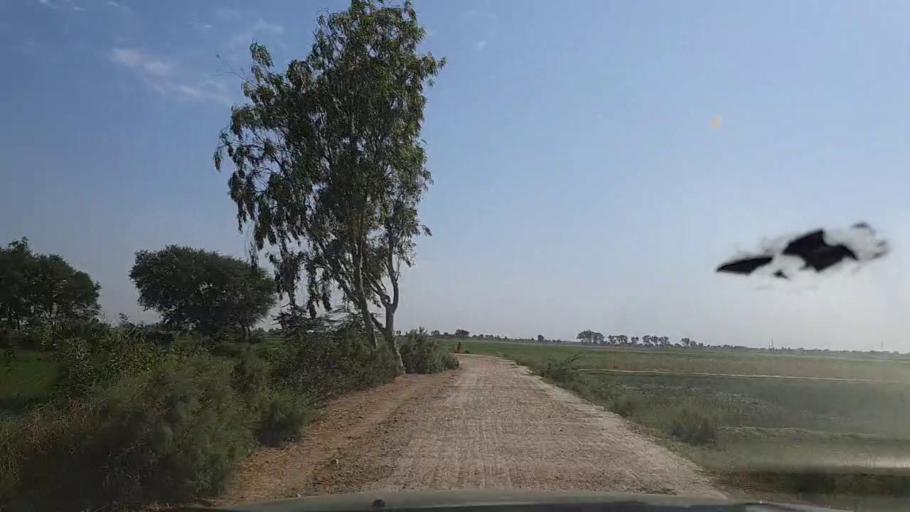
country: PK
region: Sindh
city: Daro Mehar
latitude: 24.6624
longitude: 68.0838
